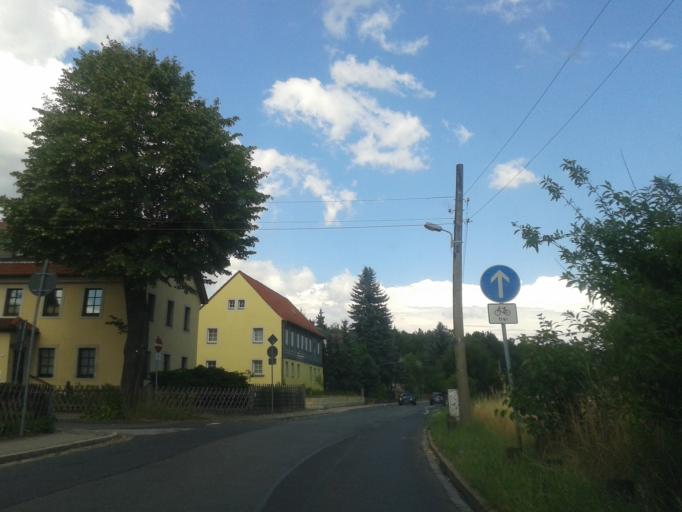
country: DE
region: Saxony
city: Radeberg
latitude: 51.0645
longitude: 13.8567
